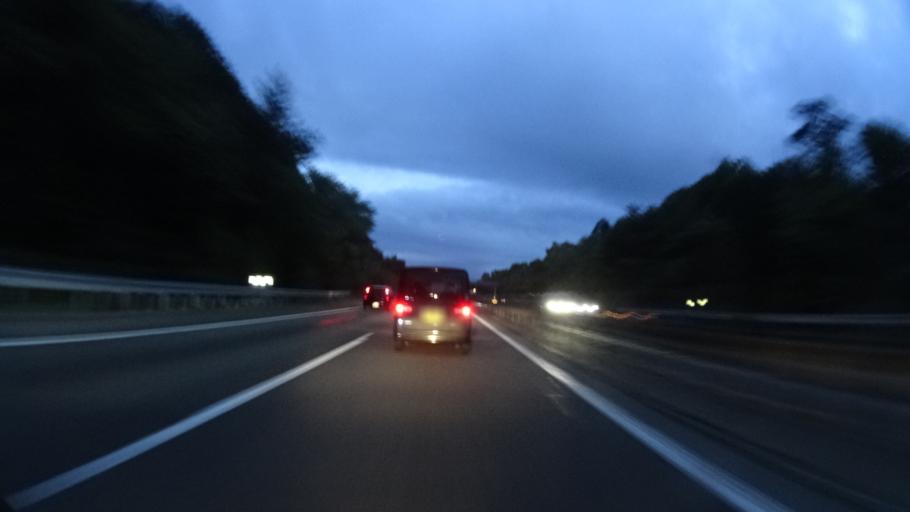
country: JP
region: Shiga Prefecture
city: Youkaichi
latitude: 35.1479
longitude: 136.2799
